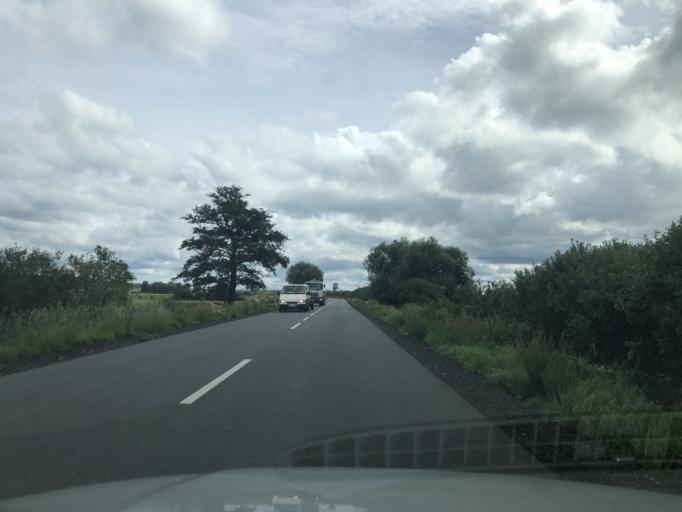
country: PL
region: Lubusz
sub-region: Powiat strzelecko-drezdenecki
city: Drezdenko
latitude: 52.8456
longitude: 15.8523
